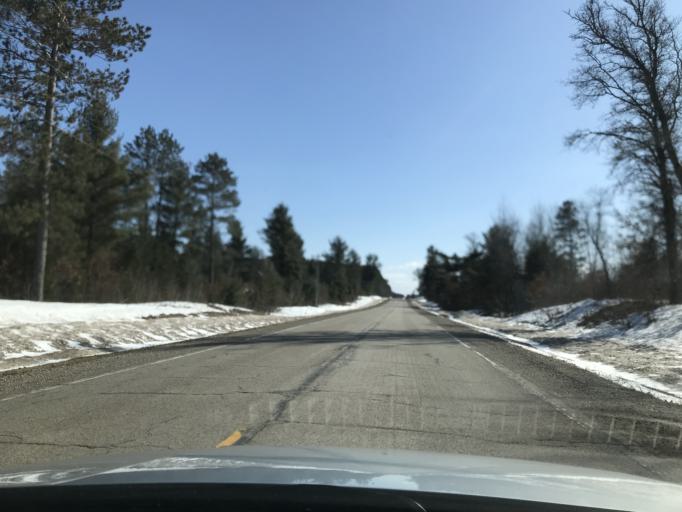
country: US
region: Wisconsin
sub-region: Marinette County
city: Niagara
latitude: 45.3879
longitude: -88.0997
